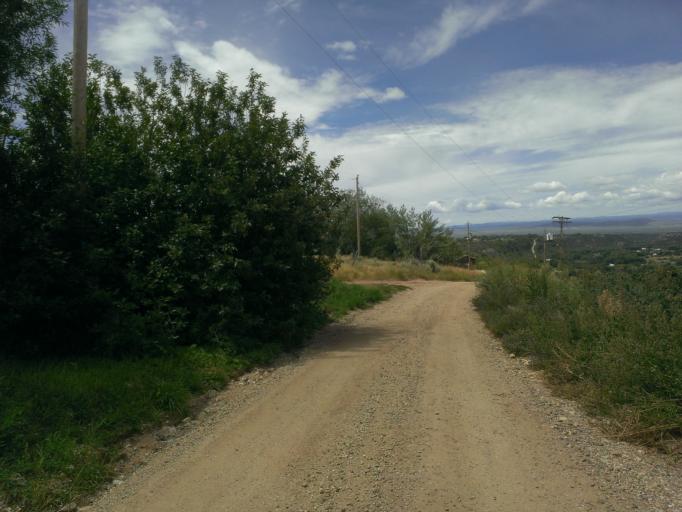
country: US
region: New Mexico
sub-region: Taos County
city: Arroyo Seco
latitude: 36.5345
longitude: -105.5625
